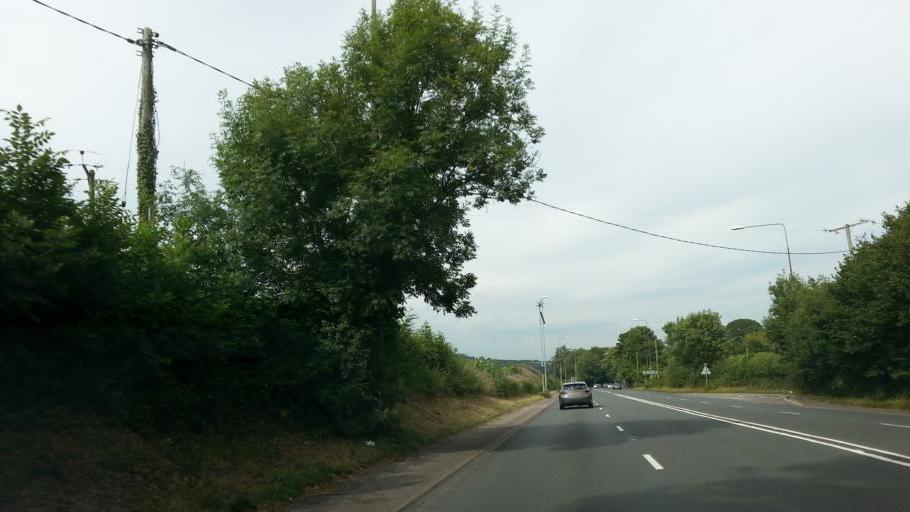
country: GB
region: Wales
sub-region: Newport
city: Marshfield
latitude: 51.5391
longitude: -3.0899
